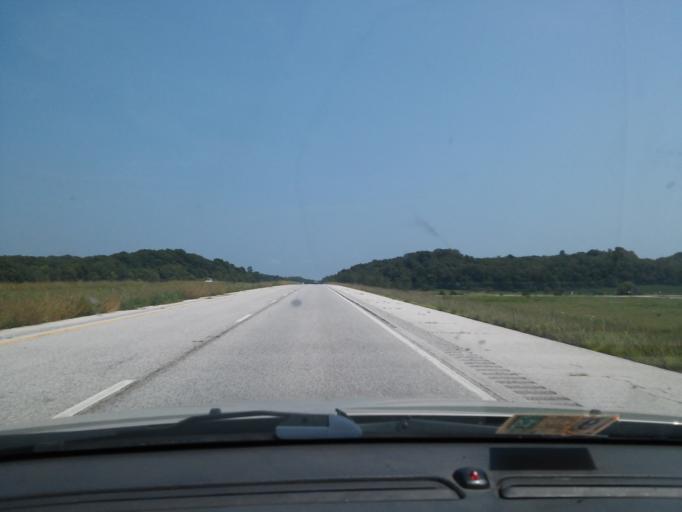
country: US
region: Illinois
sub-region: Scott County
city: Winchester
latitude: 39.6850
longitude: -90.5746
